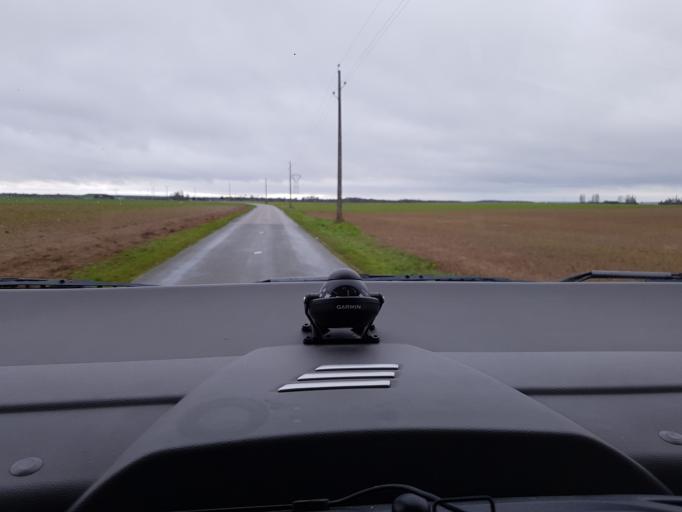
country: FR
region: Haute-Normandie
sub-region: Departement de l'Eure
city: Pont-Saint-Pierre
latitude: 49.2991
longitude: 1.3286
